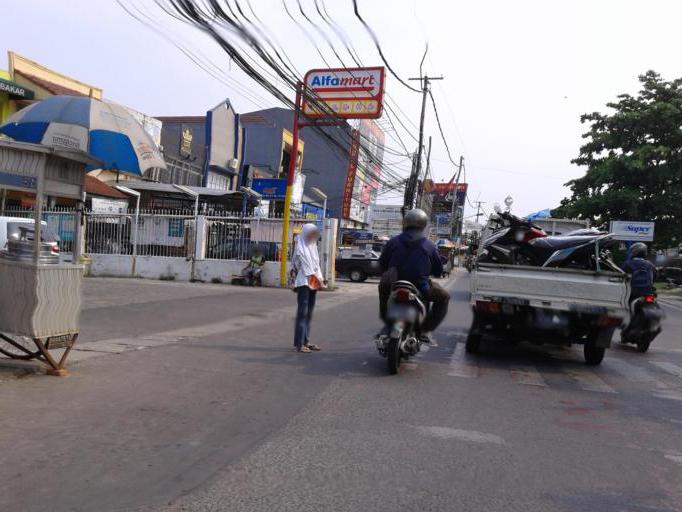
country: ID
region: West Java
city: Pamulang
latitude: -6.3362
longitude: 106.7818
